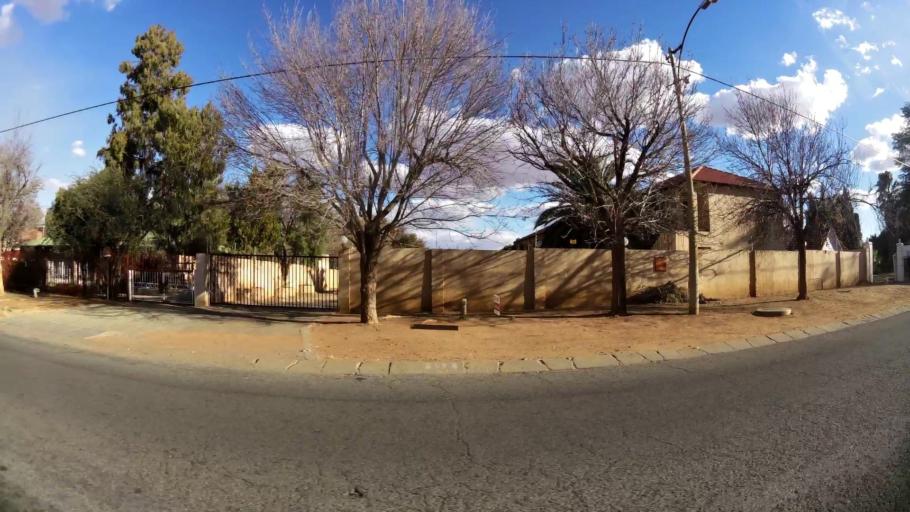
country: ZA
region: North-West
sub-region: Dr Kenneth Kaunda District Municipality
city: Klerksdorp
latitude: -26.8436
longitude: 26.6617
